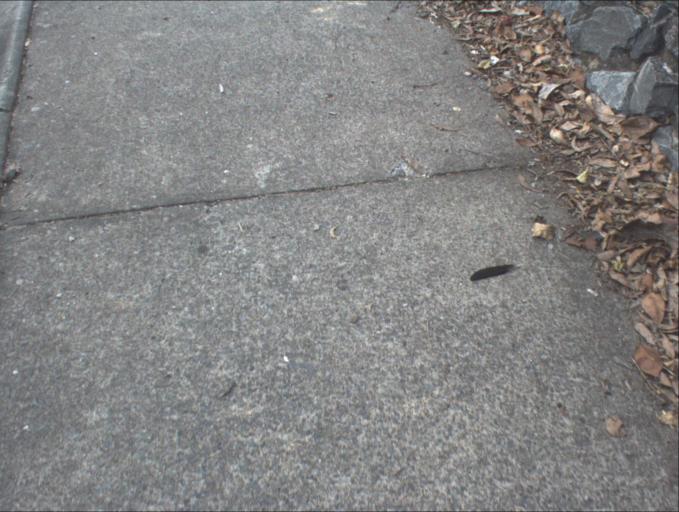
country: AU
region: Queensland
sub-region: Logan
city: Beenleigh
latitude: -27.7050
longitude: 153.1681
